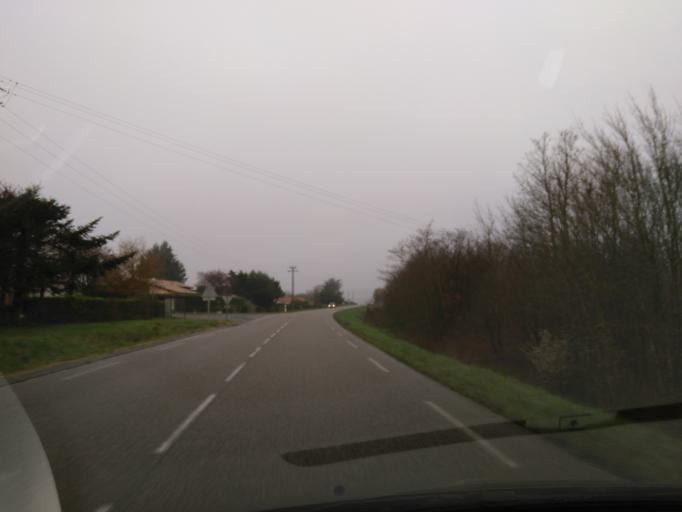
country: FR
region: Aquitaine
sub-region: Departement du Lot-et-Garonne
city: Cancon
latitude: 44.4992
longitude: 0.6672
